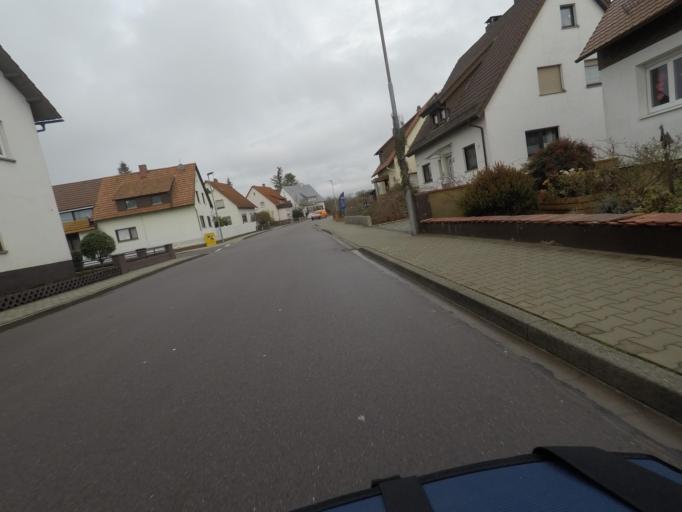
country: DE
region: Baden-Wuerttemberg
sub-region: Karlsruhe Region
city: Au am Rhein
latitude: 48.9558
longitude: 8.2415
